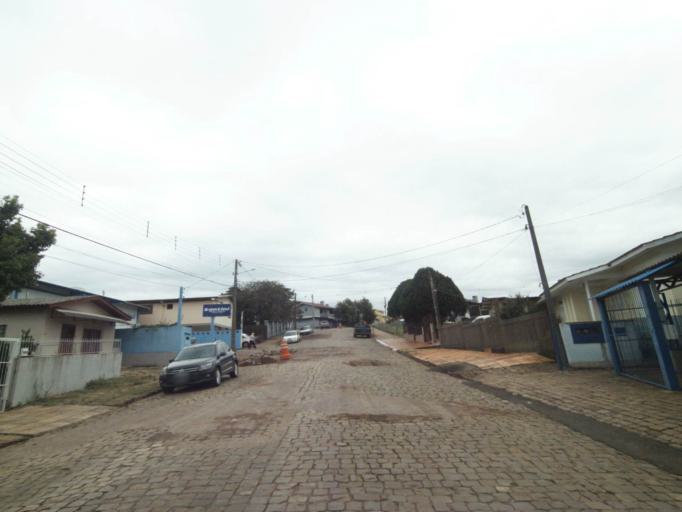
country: BR
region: Rio Grande do Sul
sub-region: Lagoa Vermelha
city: Lagoa Vermelha
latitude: -28.2157
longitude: -51.5250
